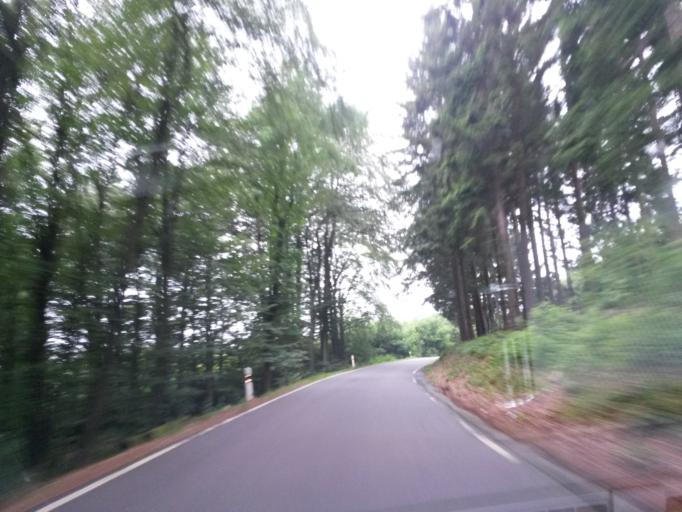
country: DE
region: North Rhine-Westphalia
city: Meinerzhagen
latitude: 51.1515
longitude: 7.6813
